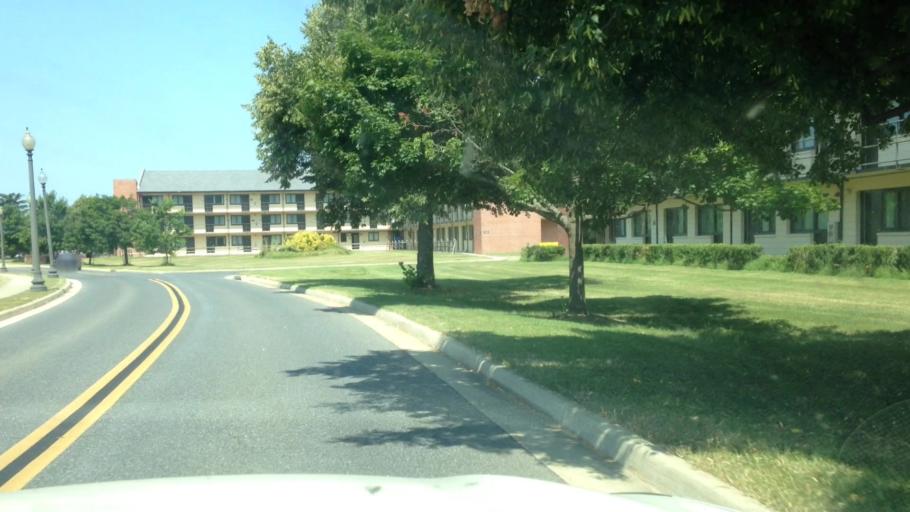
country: US
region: Maryland
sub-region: Prince George's County
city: Glassmanor
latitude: 38.8362
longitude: -77.0151
